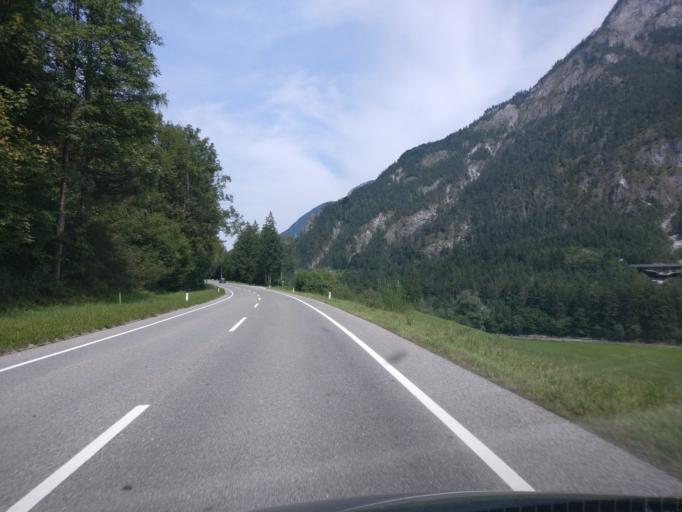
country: AT
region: Salzburg
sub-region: Politischer Bezirk Sankt Johann im Pongau
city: Werfen
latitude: 47.5093
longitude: 13.1671
